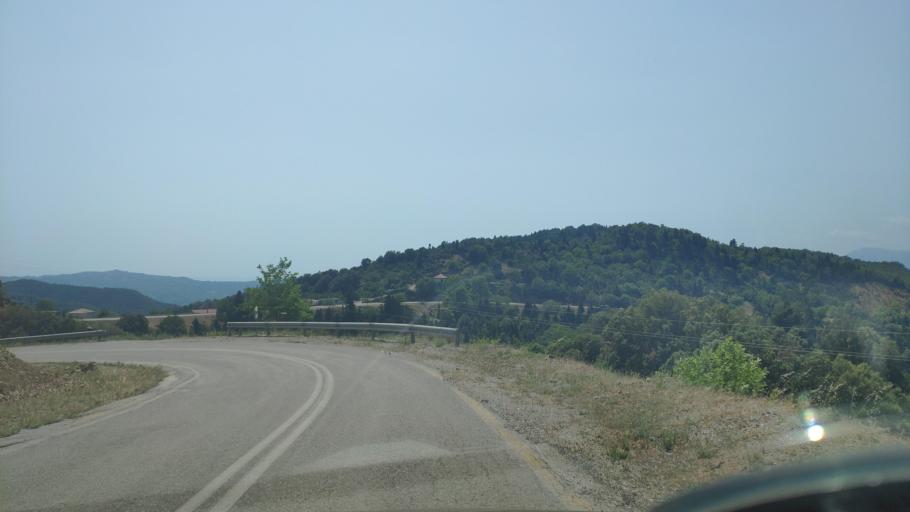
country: GR
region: Epirus
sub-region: Nomos Artas
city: Ano Kalentini
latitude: 39.2363
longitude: 21.2271
